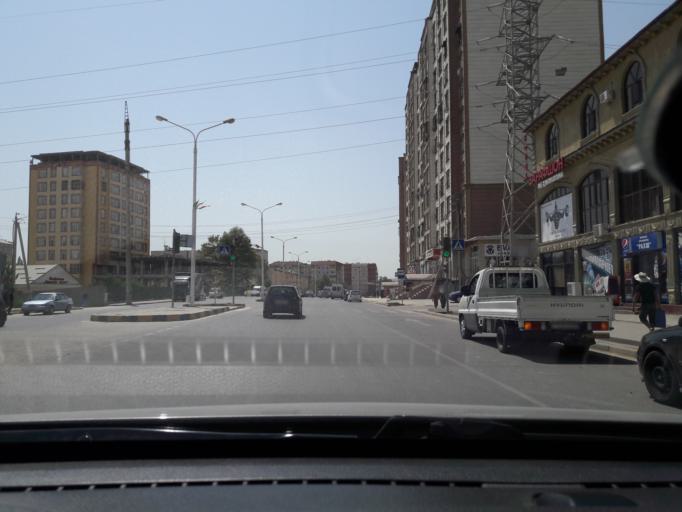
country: TJ
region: Dushanbe
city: Dushanbe
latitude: 38.5884
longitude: 68.7229
